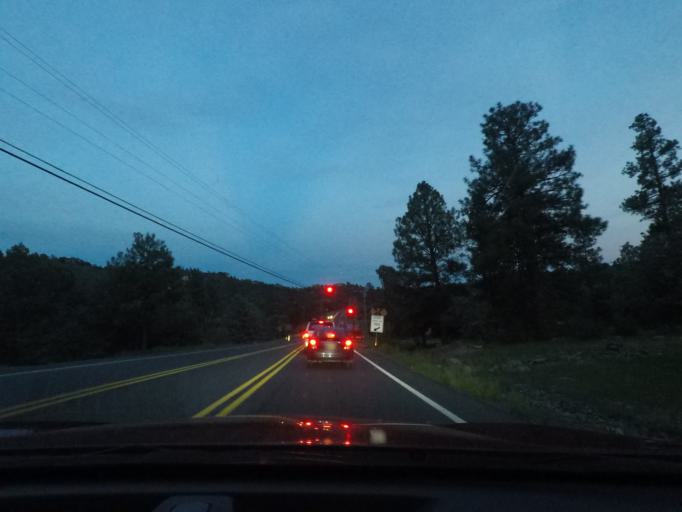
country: US
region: Arizona
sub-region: Yavapai County
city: Prescott
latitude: 34.5772
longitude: -112.5184
